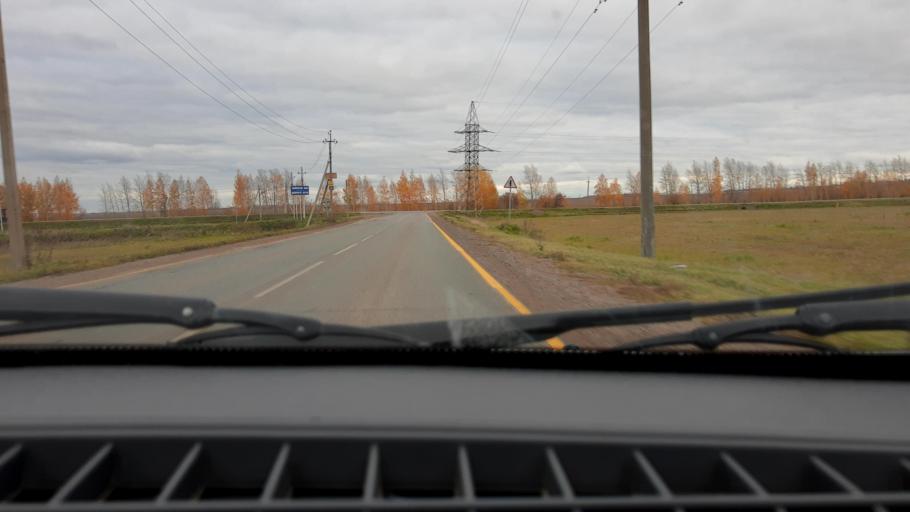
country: RU
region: Bashkortostan
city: Kabakovo
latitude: 54.5372
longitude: 56.0691
